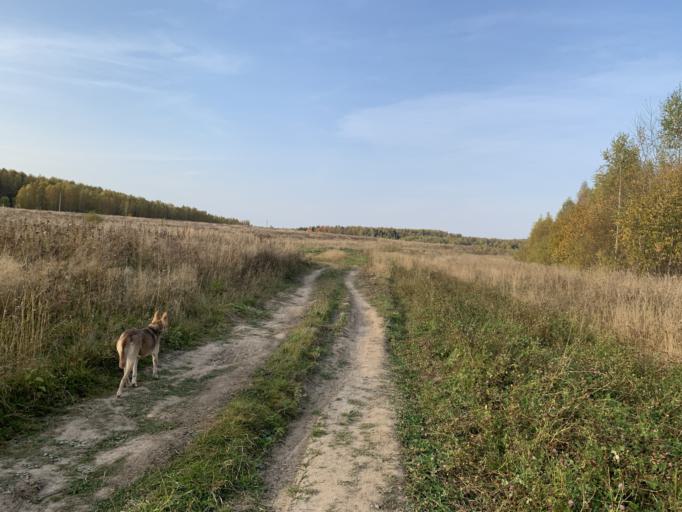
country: RU
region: Jaroslavl
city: Porech'ye-Rybnoye
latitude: 56.9827
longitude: 39.3842
